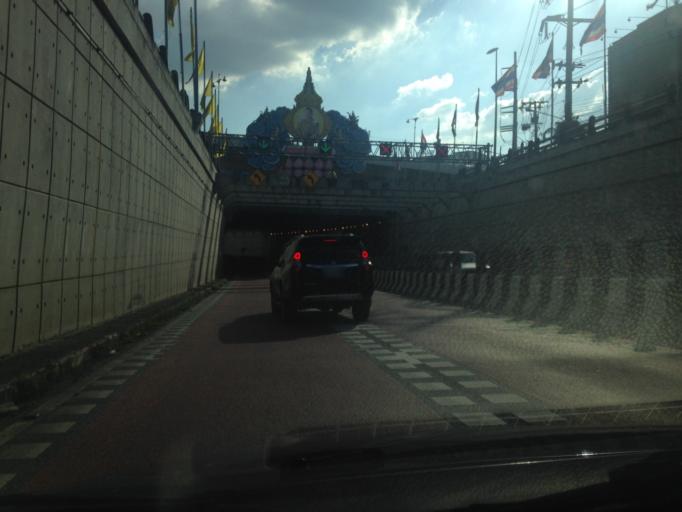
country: TH
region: Nonthaburi
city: Pak Kret
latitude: 13.9084
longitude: 100.5050
